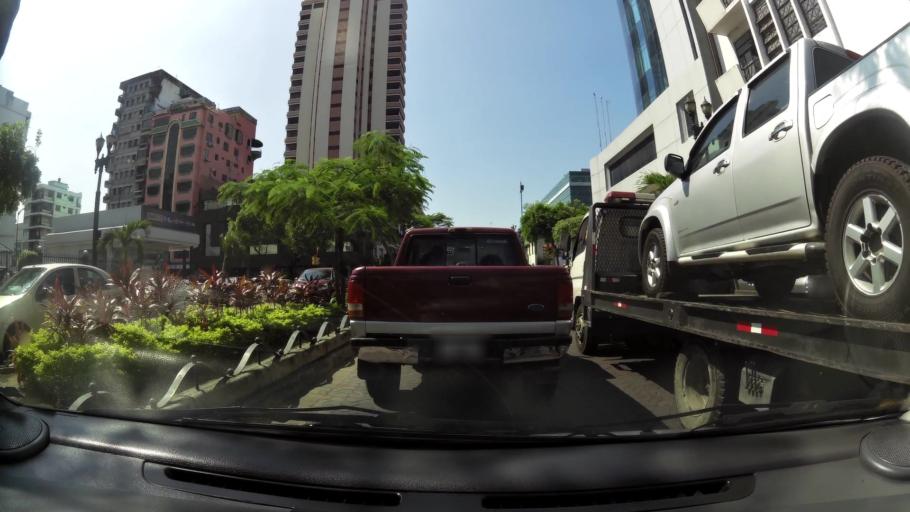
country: EC
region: Guayas
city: Guayaquil
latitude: -2.1890
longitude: -79.8903
